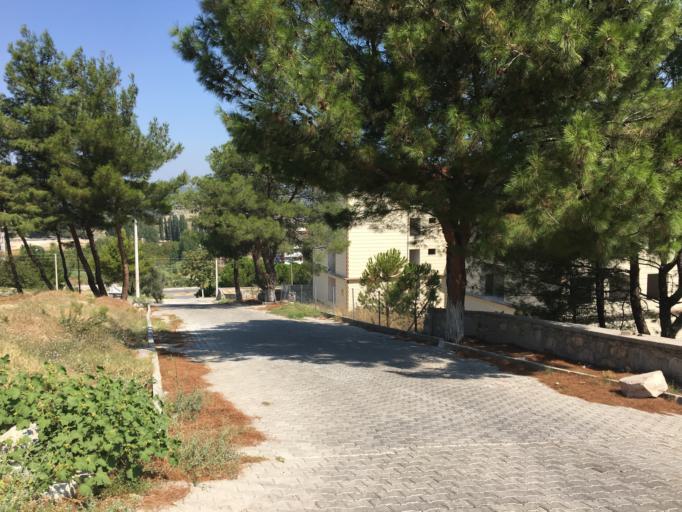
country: TR
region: Manisa
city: Soma
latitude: 39.1855
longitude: 27.5648
